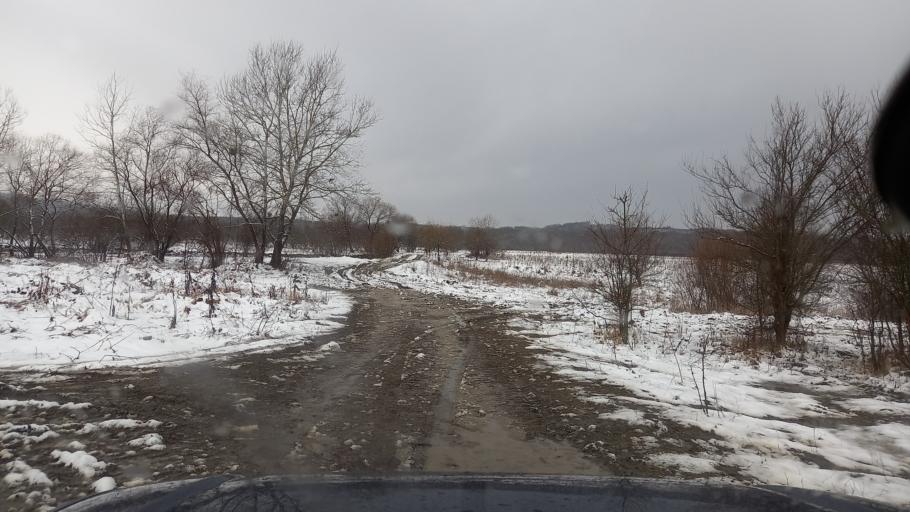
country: RU
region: Adygeya
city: Abadzekhskaya
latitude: 44.3719
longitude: 40.2509
